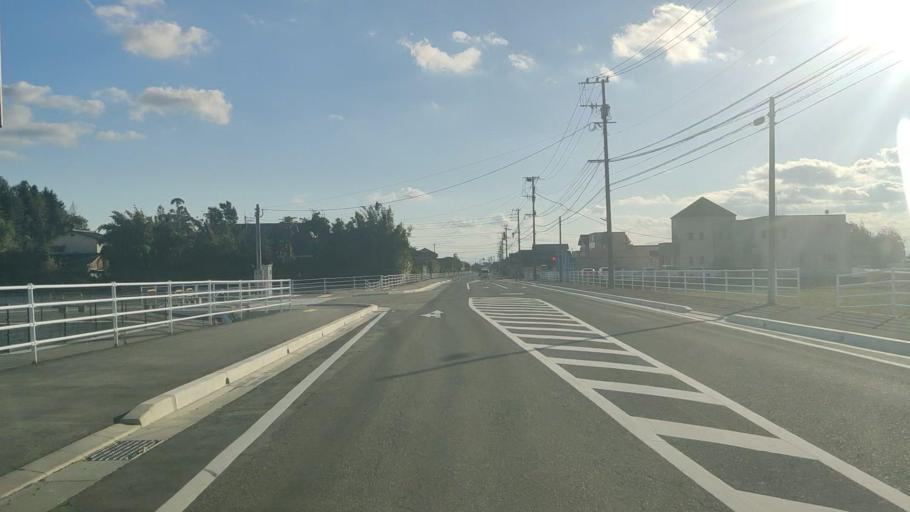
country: JP
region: Saga Prefecture
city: Saga-shi
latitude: 33.3166
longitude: 130.2665
